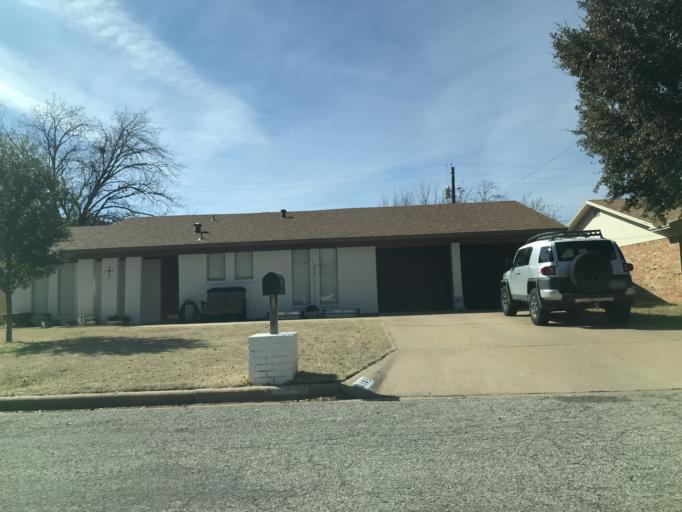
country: US
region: Texas
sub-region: Tom Green County
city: San Angelo
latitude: 31.4323
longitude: -100.4878
